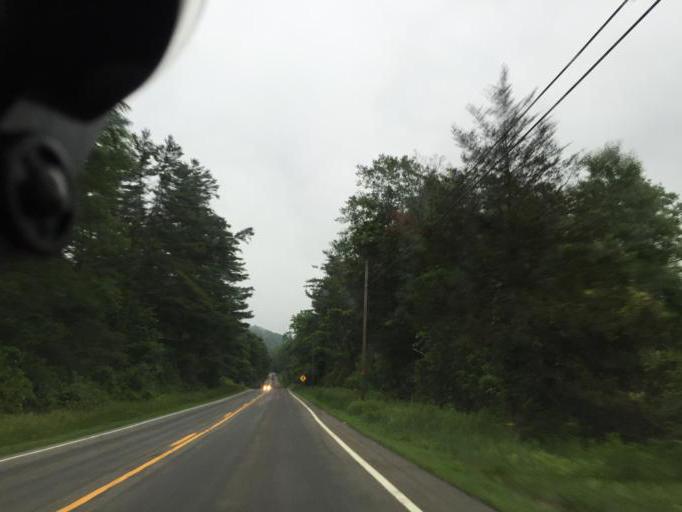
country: US
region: Connecticut
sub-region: Litchfield County
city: Canaan
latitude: 41.9285
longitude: -73.2828
